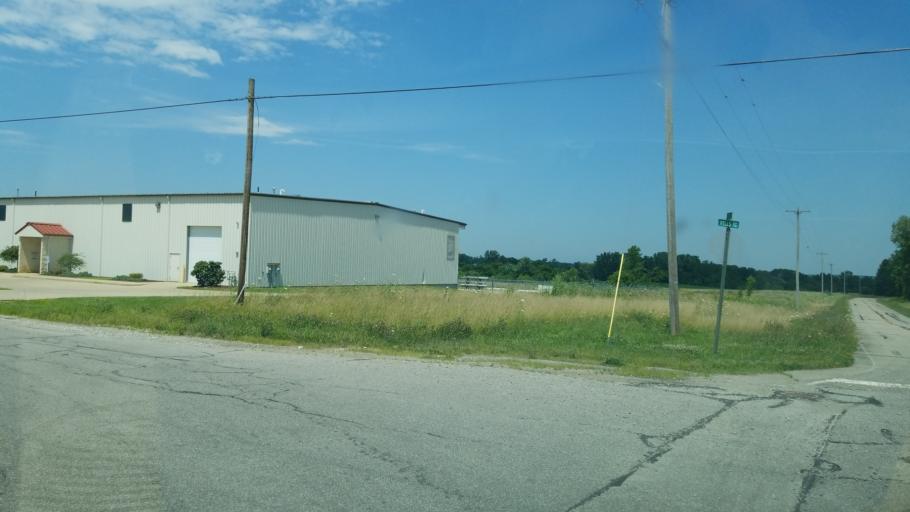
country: US
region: Ohio
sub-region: Ashland County
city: Ashland
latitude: 40.8925
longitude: -82.3394
